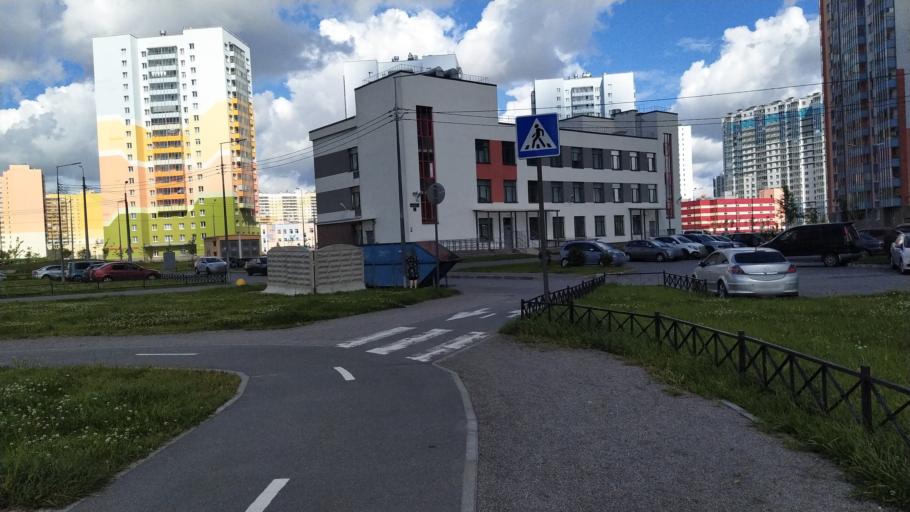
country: RU
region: Leningrad
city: Murino
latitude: 60.0290
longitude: 30.4569
